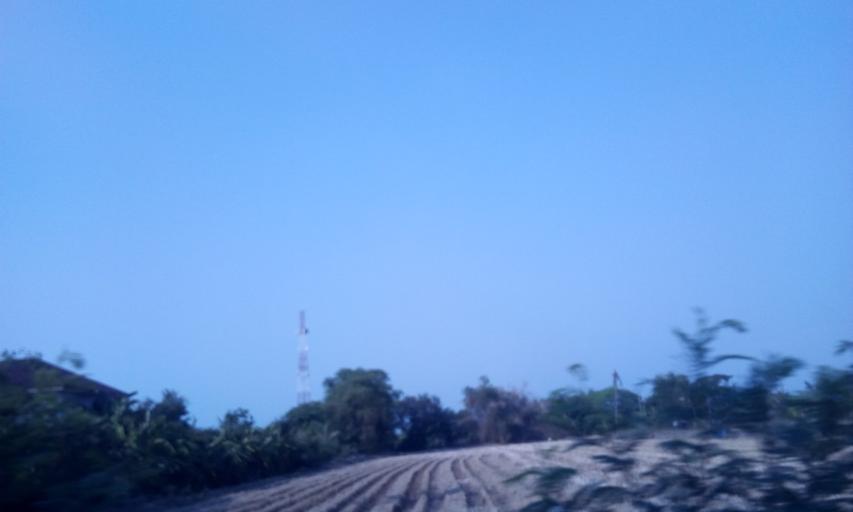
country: TH
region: Nonthaburi
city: Sai Noi
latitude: 13.9747
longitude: 100.3143
